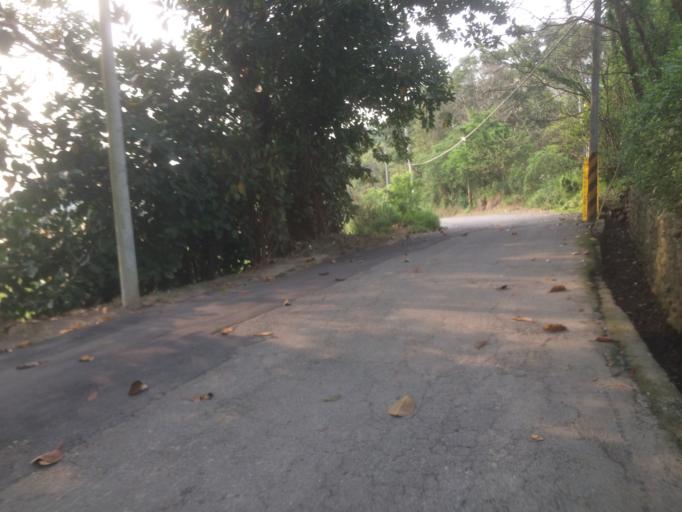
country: TW
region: Taiwan
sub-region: Hsinchu
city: Hsinchu
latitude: 24.7627
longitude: 120.9769
